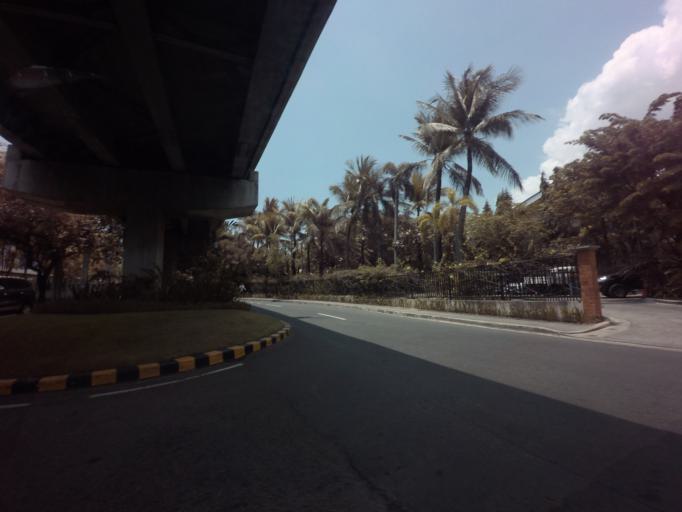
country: PH
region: Metro Manila
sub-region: Makati City
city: Makati City
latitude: 14.5613
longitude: 121.0397
